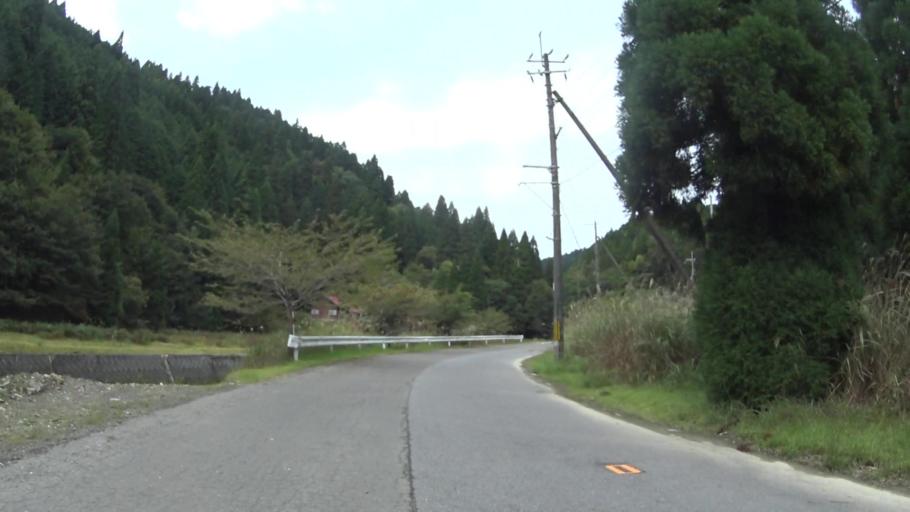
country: JP
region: Shiga Prefecture
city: Kitahama
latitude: 35.2653
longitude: 135.7440
